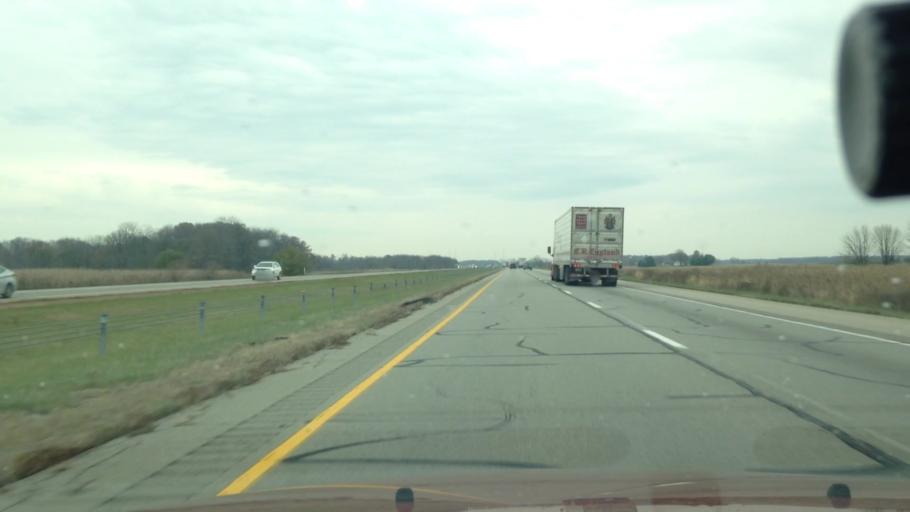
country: US
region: Indiana
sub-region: Henry County
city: New Castle
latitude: 39.8523
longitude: -85.2893
